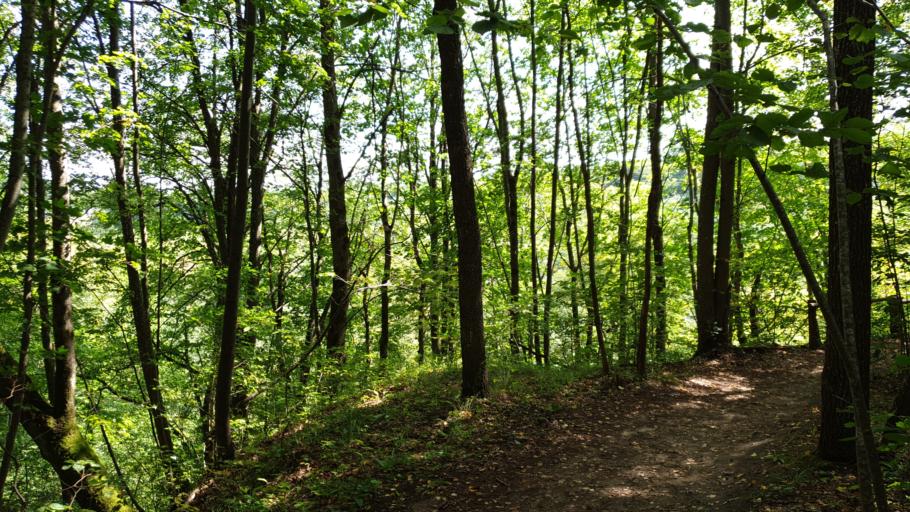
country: LT
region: Vilnius County
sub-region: Vilniaus Rajonas
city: Vievis
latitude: 54.8251
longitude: 24.9398
